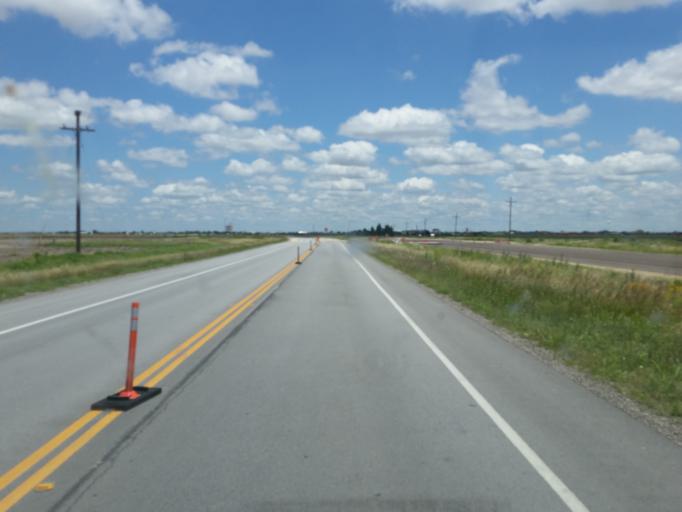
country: US
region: Texas
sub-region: Nolan County
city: Roscoe
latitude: 32.4557
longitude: -100.5617
